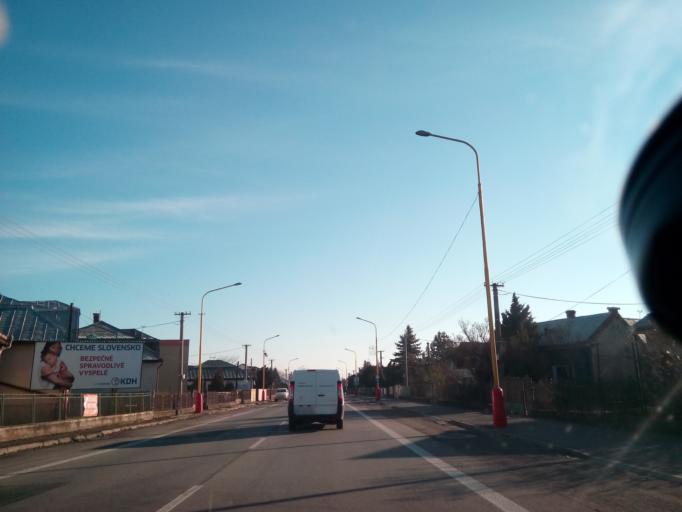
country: SK
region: Kosicky
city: Secovce
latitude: 48.7033
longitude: 21.6797
